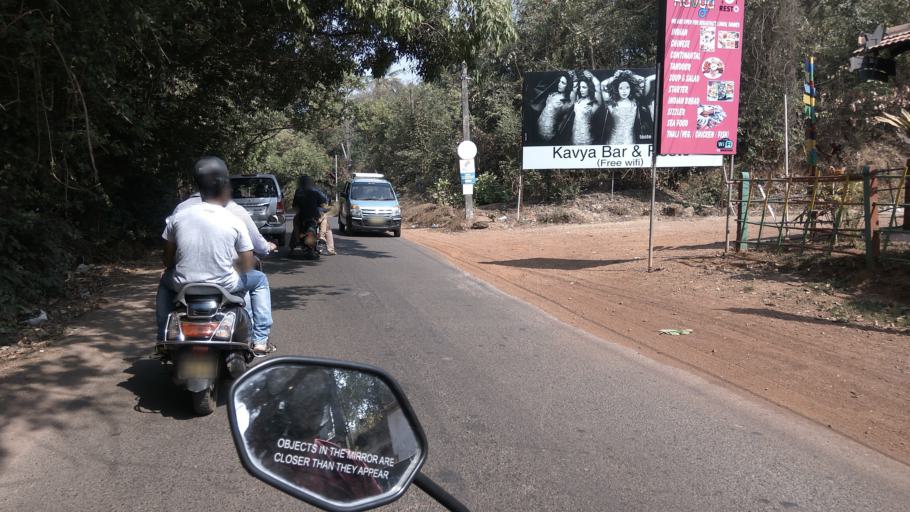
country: IN
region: Goa
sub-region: North Goa
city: Vagator
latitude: 15.5794
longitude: 73.7590
